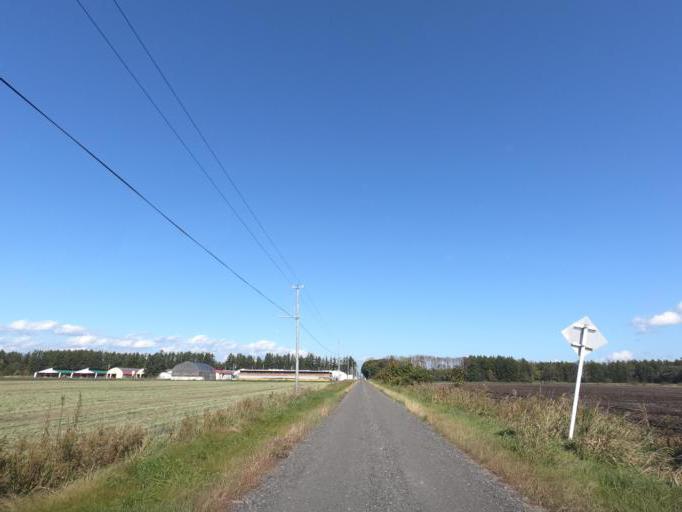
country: JP
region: Hokkaido
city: Otofuke
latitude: 43.0720
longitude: 143.2589
